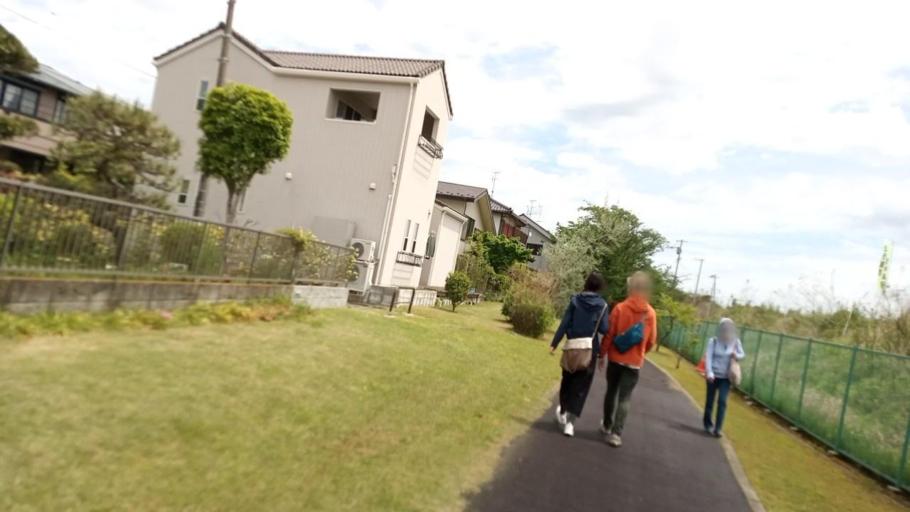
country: JP
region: Chiba
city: Abiko
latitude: 35.8636
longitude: 140.0209
